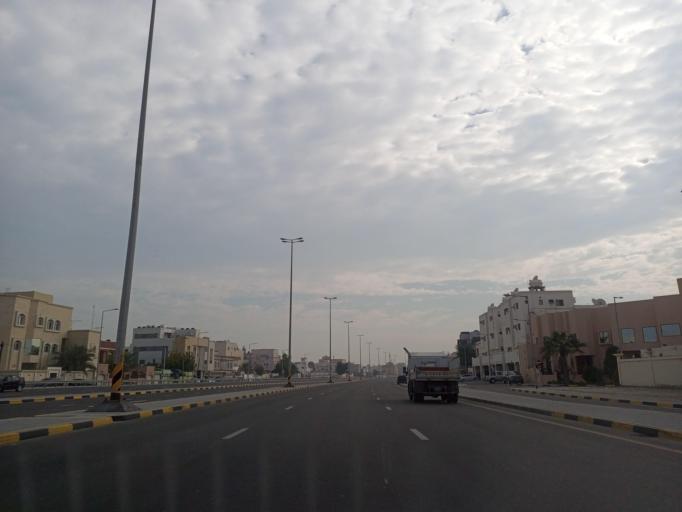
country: BH
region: Muharraq
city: Al Hadd
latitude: 26.2471
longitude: 50.6414
